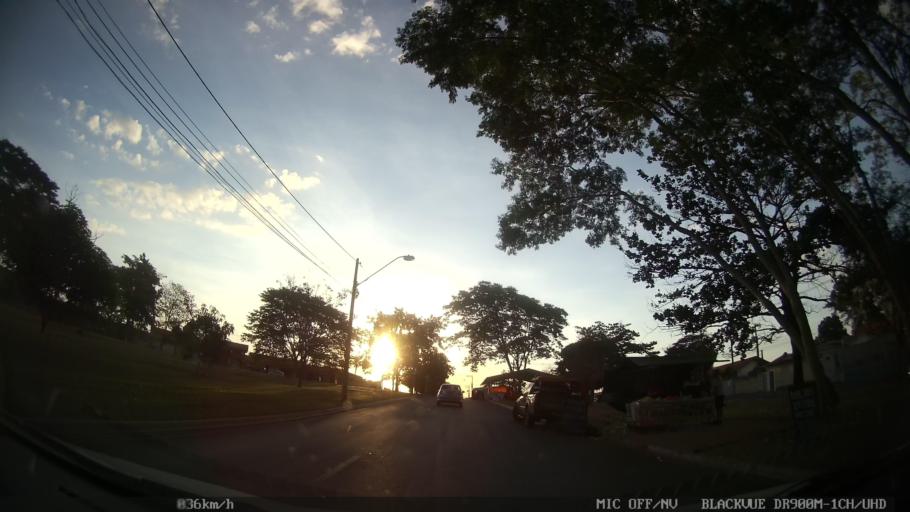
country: BR
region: Sao Paulo
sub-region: Ribeirao Preto
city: Ribeirao Preto
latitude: -21.1572
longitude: -47.8380
